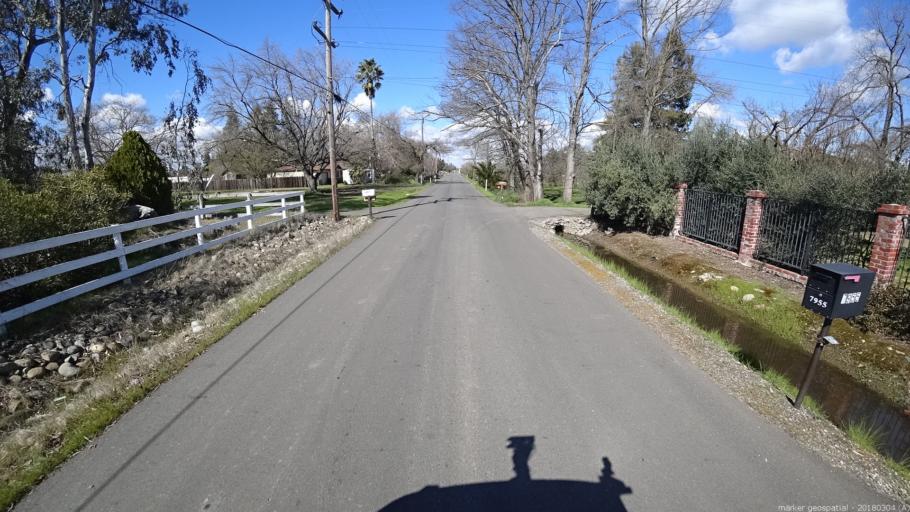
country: US
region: California
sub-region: Sacramento County
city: Vineyard
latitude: 38.4689
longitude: -121.3301
